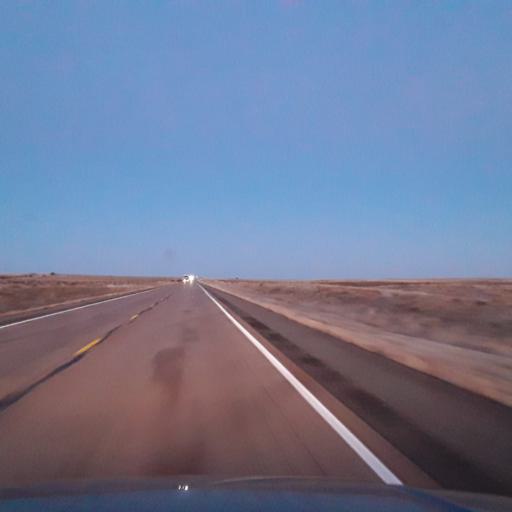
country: US
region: New Mexico
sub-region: Guadalupe County
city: Santa Rosa
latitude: 34.7628
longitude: -104.9839
